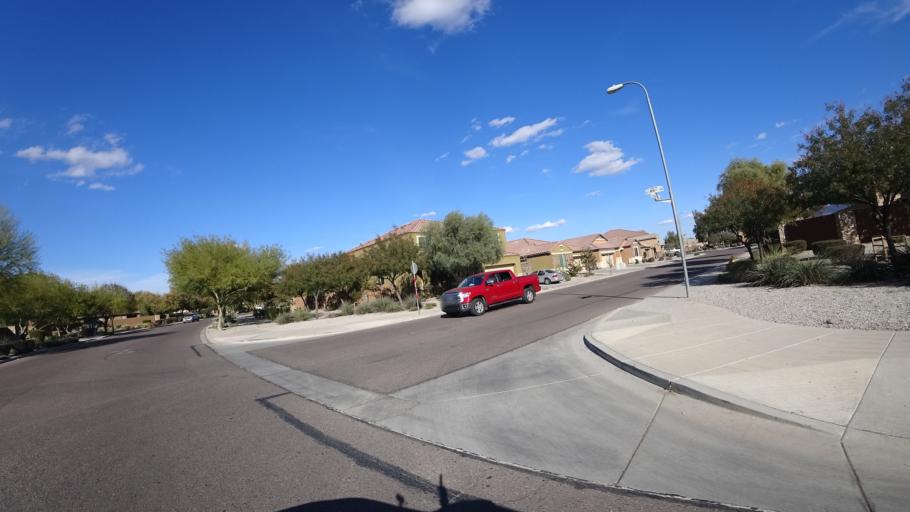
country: US
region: Arizona
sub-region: Maricopa County
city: Tolleson
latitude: 33.4180
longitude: -112.2521
